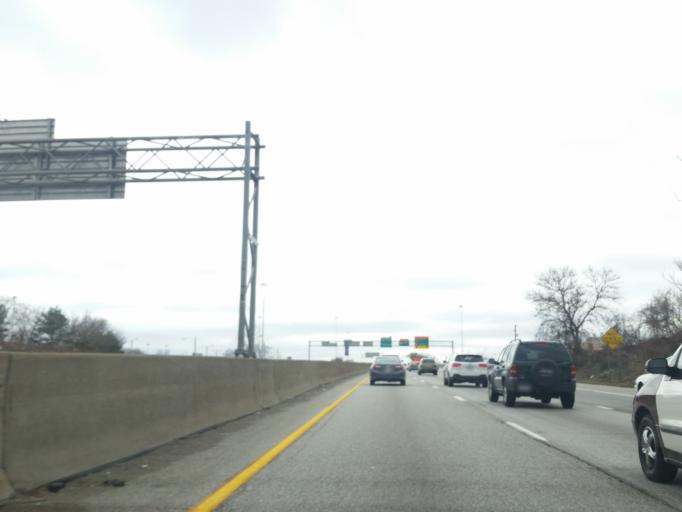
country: US
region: Ohio
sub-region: Cuyahoga County
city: Cleveland
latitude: 41.4981
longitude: -81.6743
